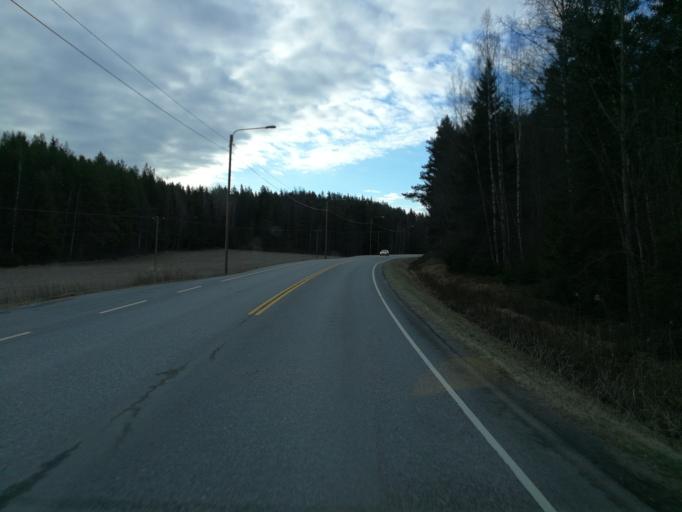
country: FI
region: Varsinais-Suomi
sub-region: Turku
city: Paimio
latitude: 60.4314
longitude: 22.6093
